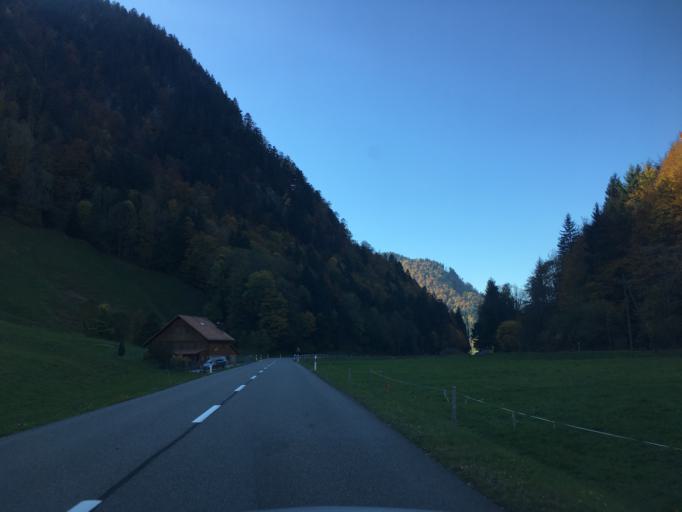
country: CH
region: Fribourg
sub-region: Gruyere District
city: Charmey
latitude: 46.5984
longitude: 7.2183
